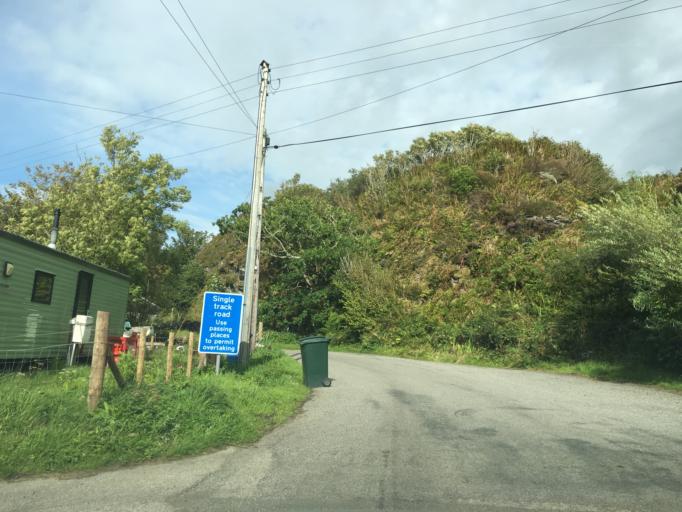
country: GB
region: Scotland
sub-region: Argyll and Bute
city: Oban
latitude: 56.2689
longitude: -5.6284
